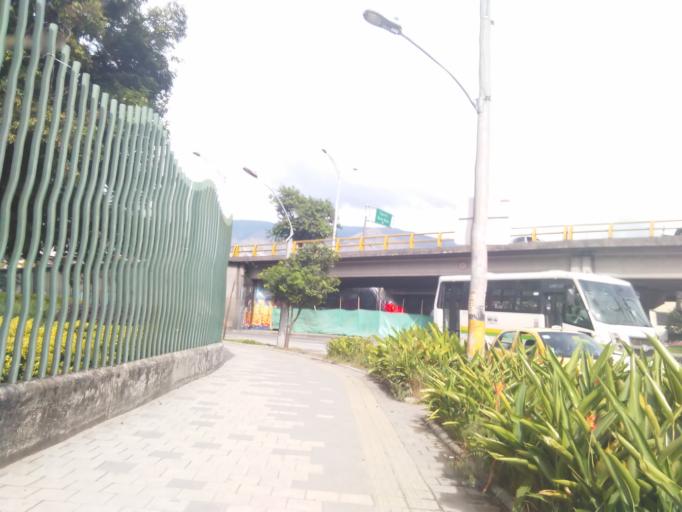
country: CO
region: Antioquia
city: Medellin
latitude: 6.2401
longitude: -75.5759
